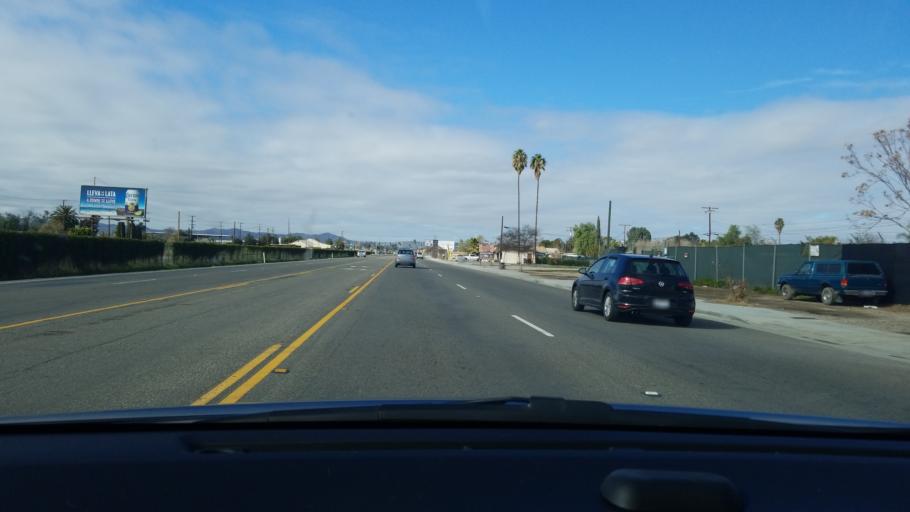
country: US
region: California
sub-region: Riverside County
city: Romoland
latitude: 33.7463
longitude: -117.1761
